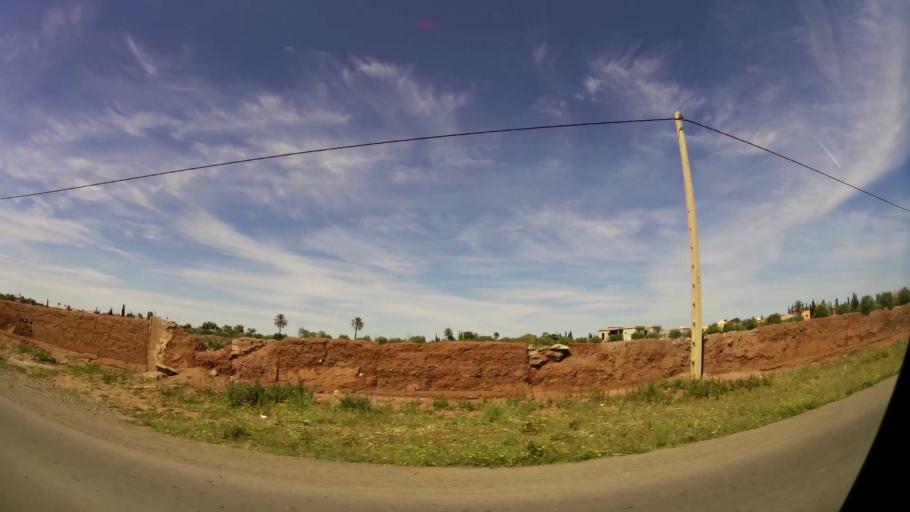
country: MA
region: Marrakech-Tensift-Al Haouz
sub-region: Marrakech
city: Marrakesh
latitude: 31.6120
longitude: -7.9436
